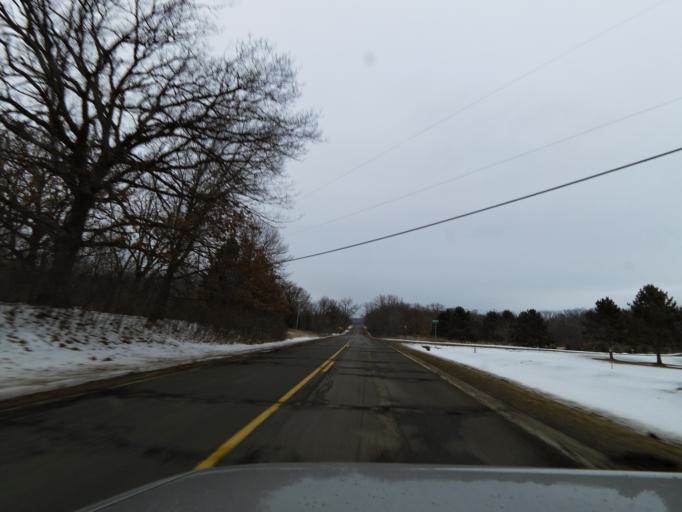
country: US
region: Minnesota
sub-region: Washington County
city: Afton
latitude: 44.8511
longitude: -92.7973
